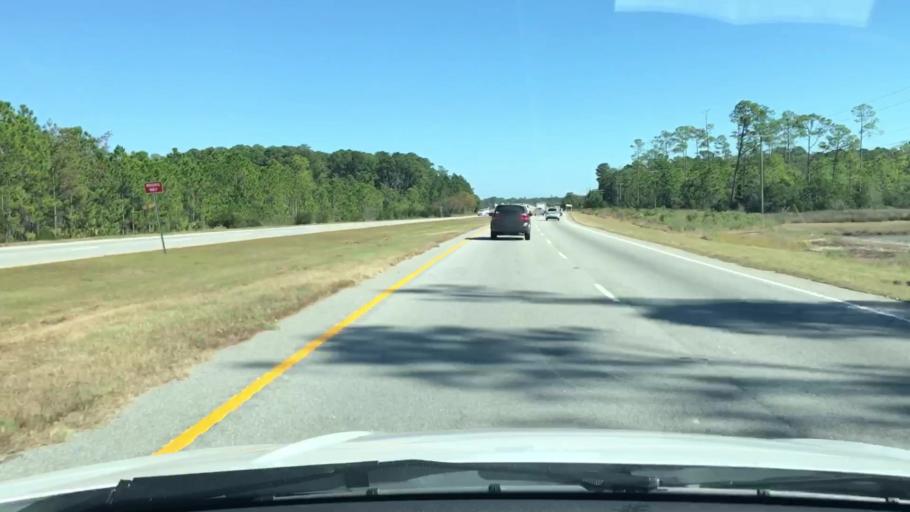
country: US
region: South Carolina
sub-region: Beaufort County
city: Laurel Bay
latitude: 32.3737
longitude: -80.8447
